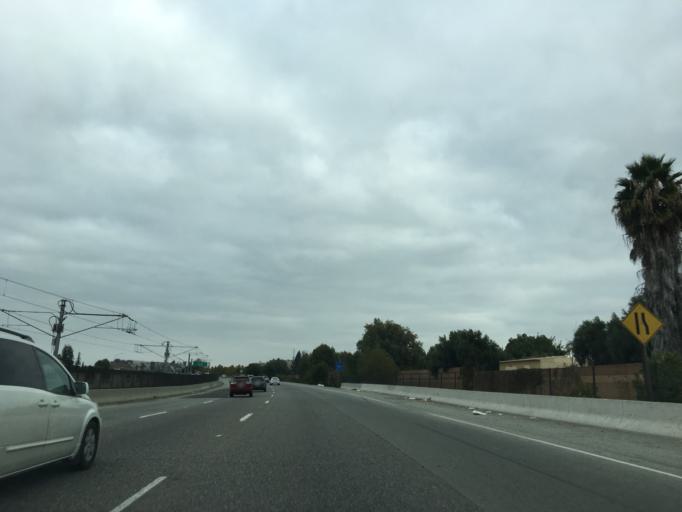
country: US
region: California
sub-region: Santa Clara County
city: Seven Trees
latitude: 37.2671
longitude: -121.8592
